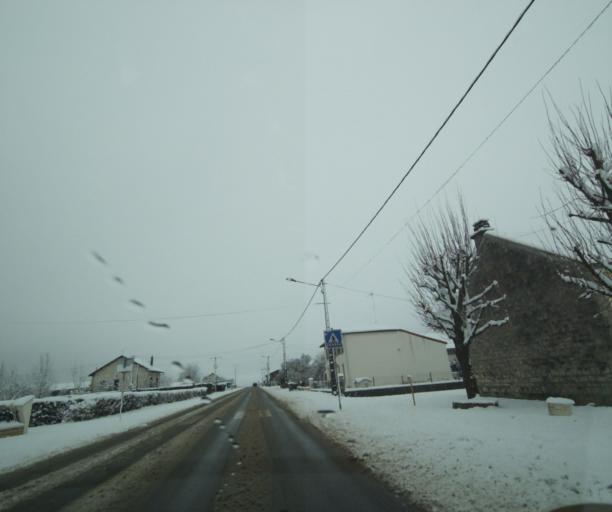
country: FR
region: Champagne-Ardenne
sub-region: Departement de la Haute-Marne
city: Wassy
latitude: 48.5282
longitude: 4.9281
